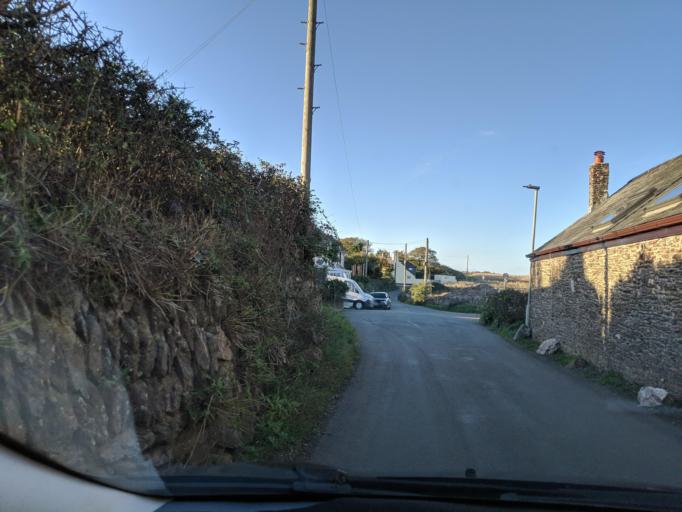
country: GB
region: England
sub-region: Devon
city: Wembury
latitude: 50.3322
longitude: -4.1038
